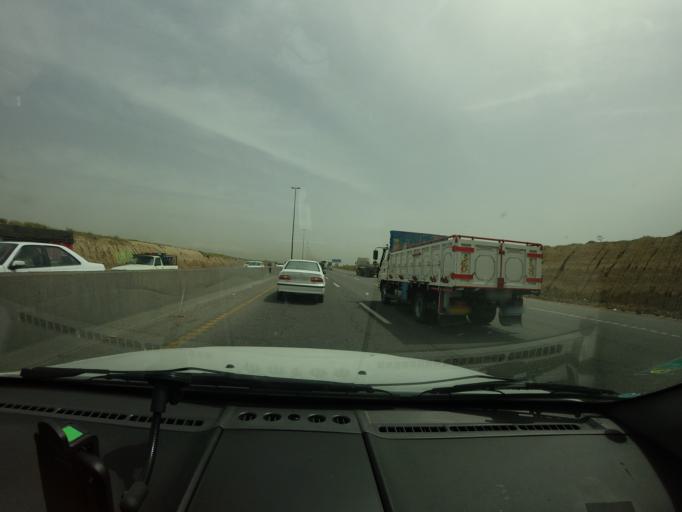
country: IR
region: Tehran
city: Eslamshahr
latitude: 35.5980
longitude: 51.1840
